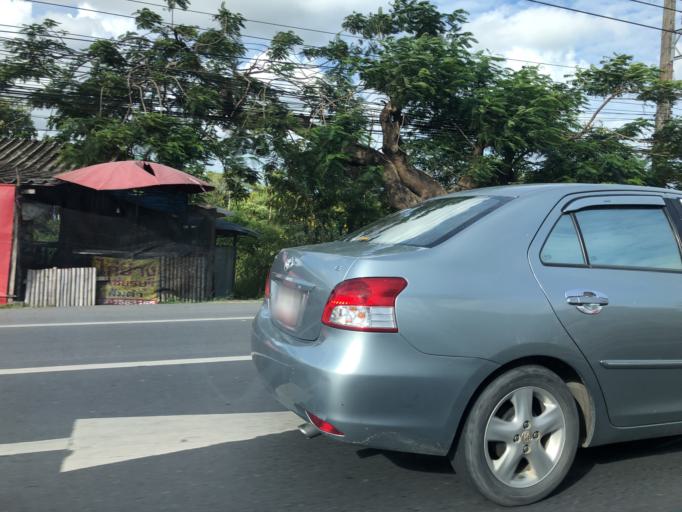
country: TH
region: Phuket
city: Thalang
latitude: 8.0029
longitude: 98.3459
